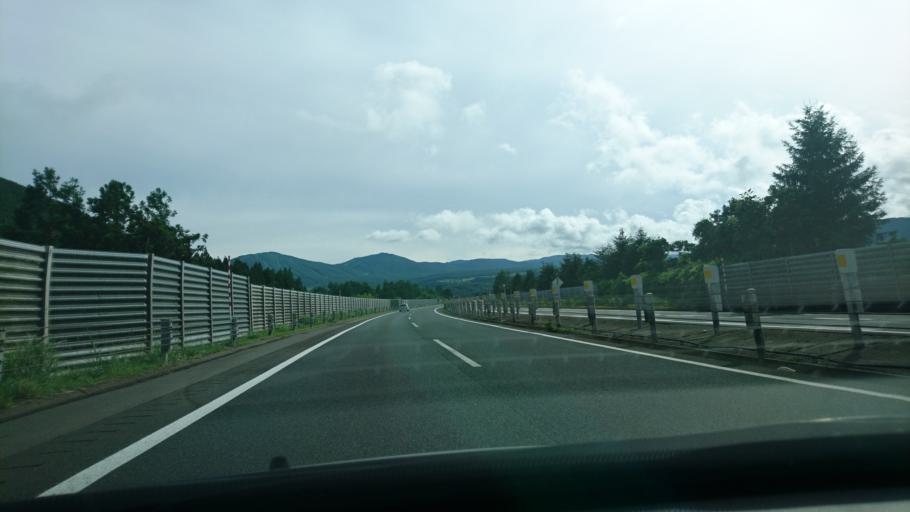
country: JP
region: Akita
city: Hanawa
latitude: 40.0357
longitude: 140.9891
